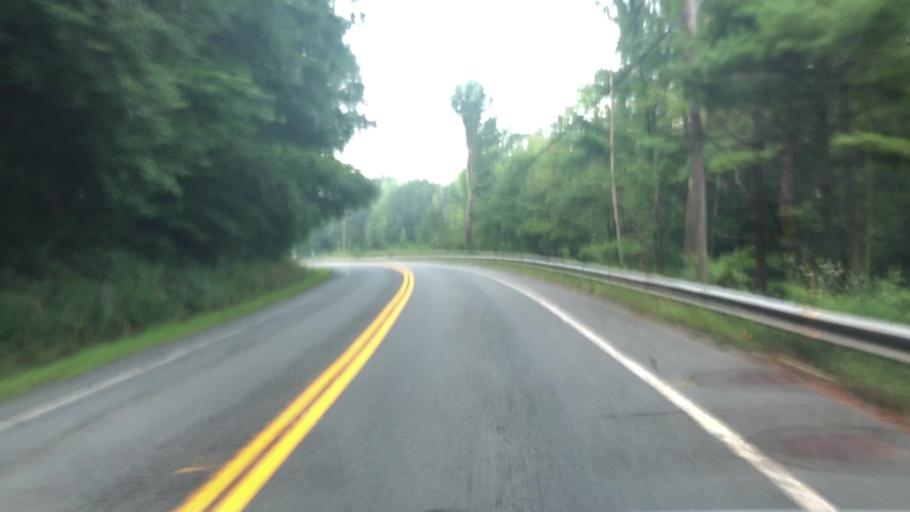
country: US
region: Massachusetts
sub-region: Franklin County
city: Buckland
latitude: 42.5808
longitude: -72.7993
